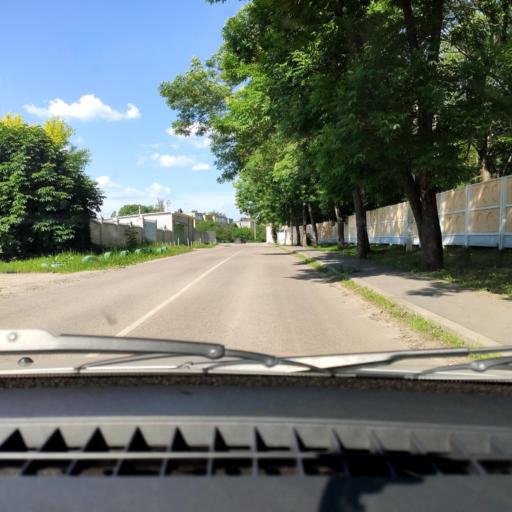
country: RU
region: Voronezj
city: Ramon'
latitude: 51.8242
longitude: 39.2613
